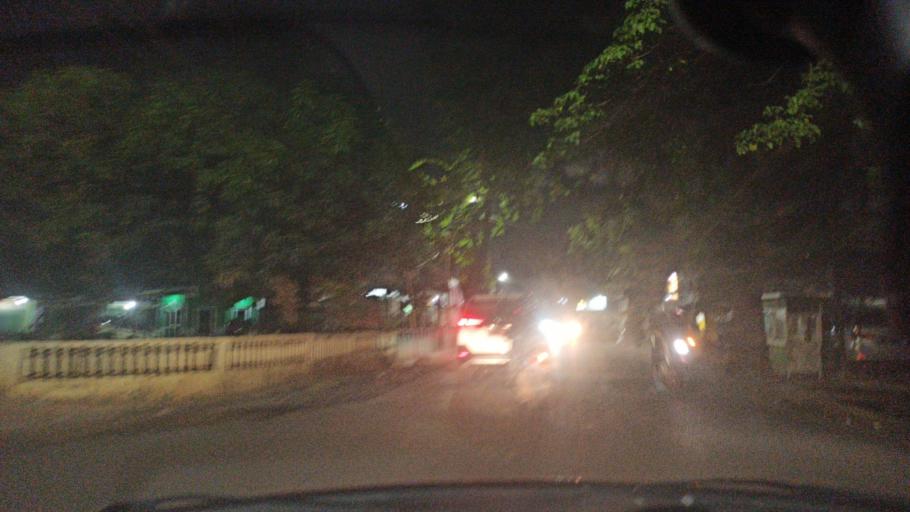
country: ID
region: South Sumatra
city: Palembang
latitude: -2.9315
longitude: 104.7904
